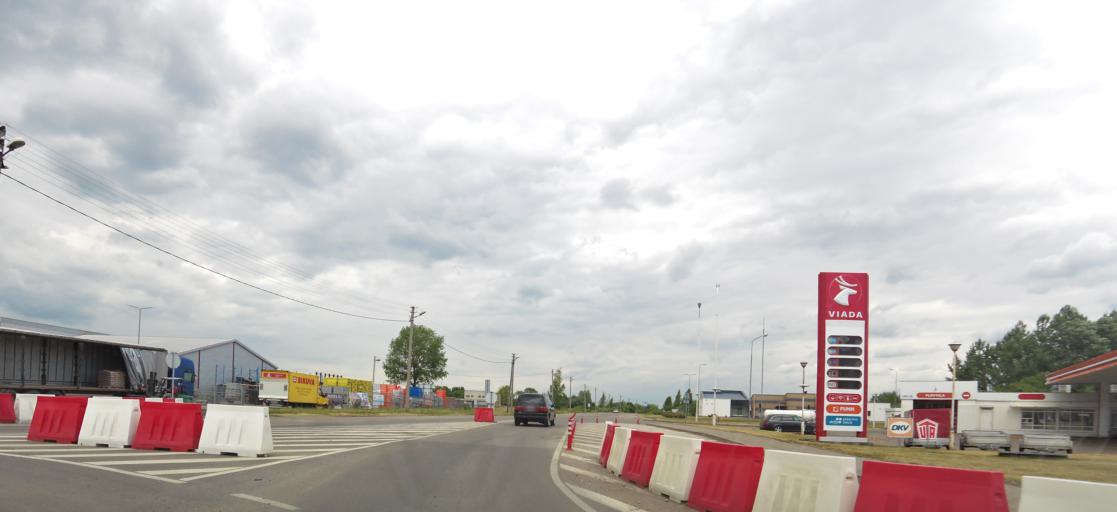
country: LT
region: Vilnius County
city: Ukmerge
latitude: 55.2456
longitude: 24.7427
